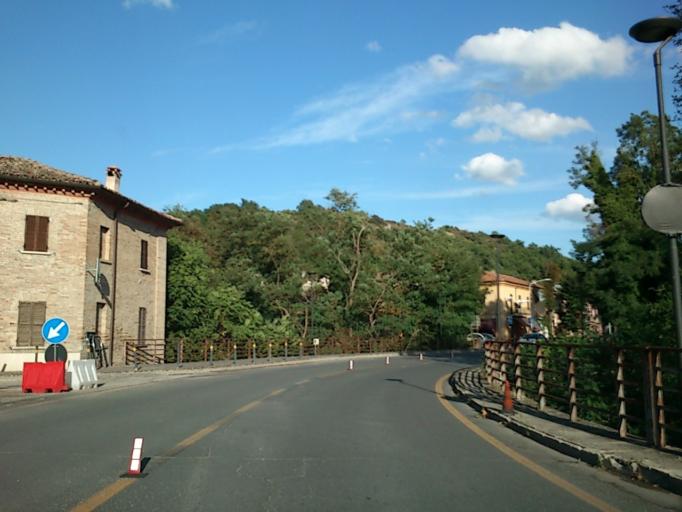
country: IT
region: The Marches
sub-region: Provincia di Pesaro e Urbino
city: Urbania
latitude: 43.6661
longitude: 12.5238
